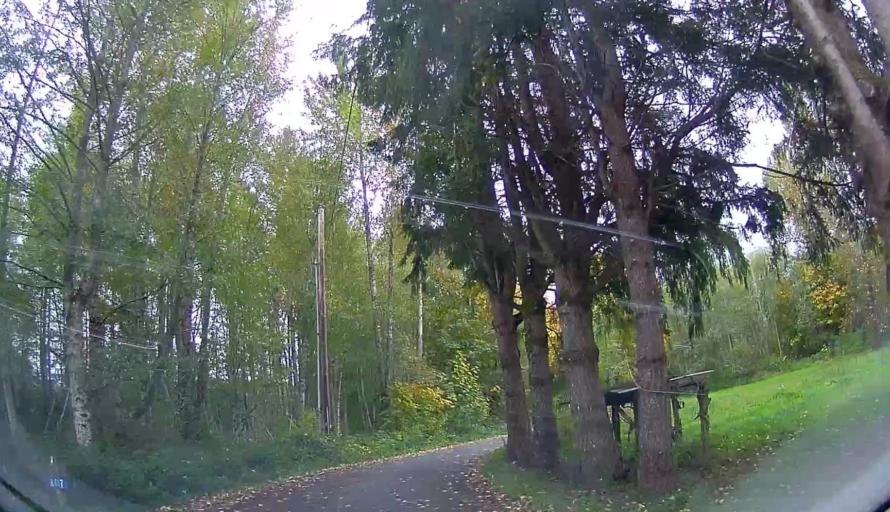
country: US
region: Washington
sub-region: Skagit County
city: Sedro-Woolley
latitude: 48.5226
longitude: -122.0882
